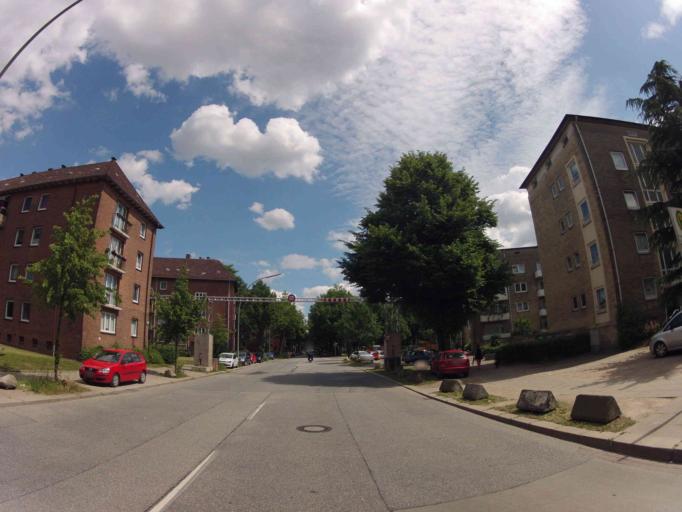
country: DE
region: Hamburg
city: Rothenburgsort
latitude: 53.5335
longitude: 10.0468
